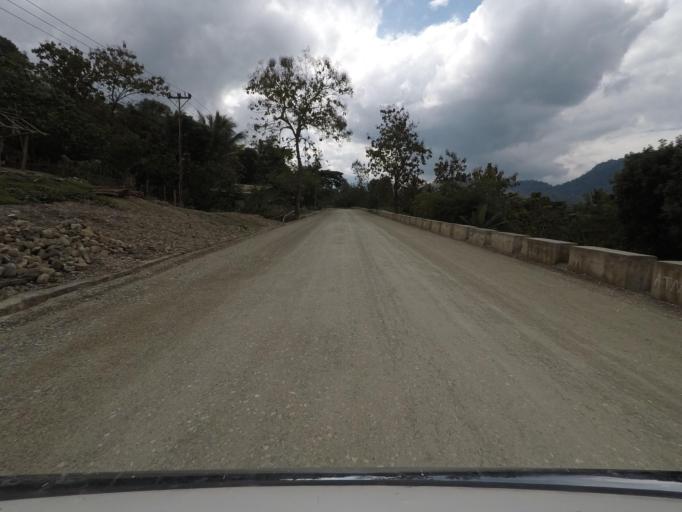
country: TL
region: Viqueque
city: Viqueque
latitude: -8.8033
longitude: 126.3789
